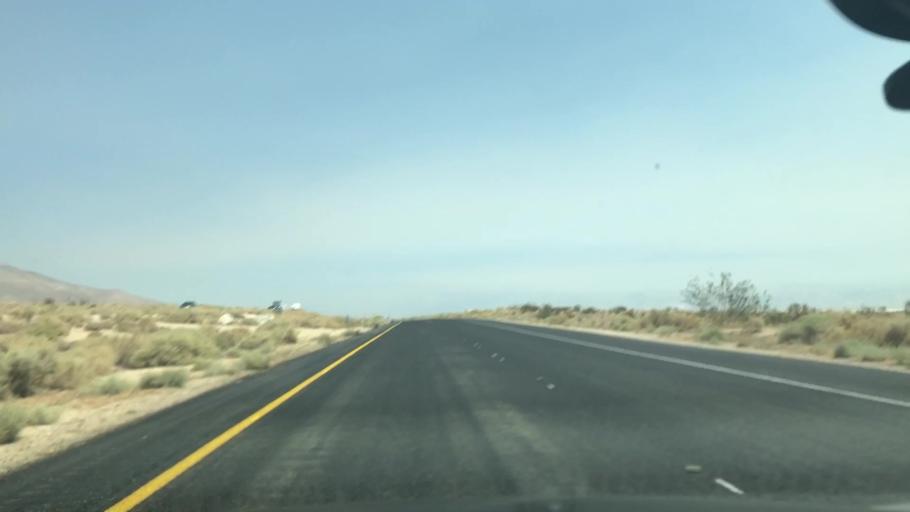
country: US
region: California
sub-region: Inyo County
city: Lone Pine
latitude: 36.3887
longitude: -118.0239
